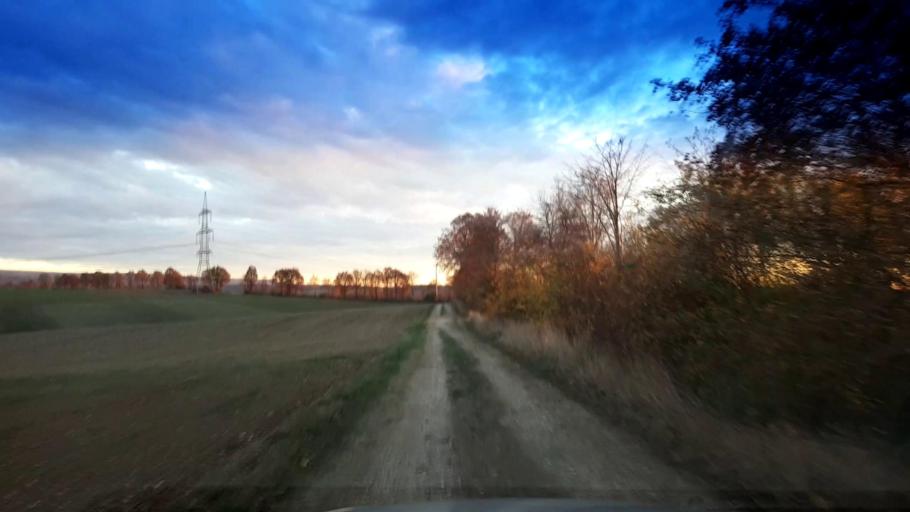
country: DE
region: Bavaria
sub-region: Upper Franconia
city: Memmelsdorf
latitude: 49.9624
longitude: 10.9766
